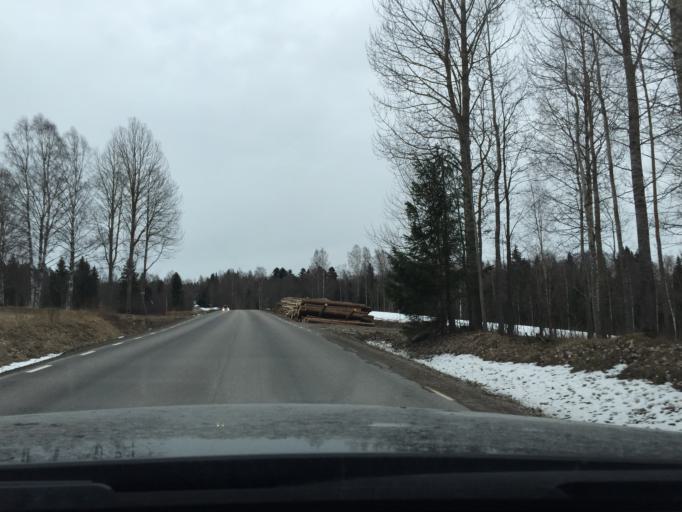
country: SE
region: Gaevleborg
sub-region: Sandvikens Kommun
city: Jarbo
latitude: 60.7612
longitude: 16.5273
